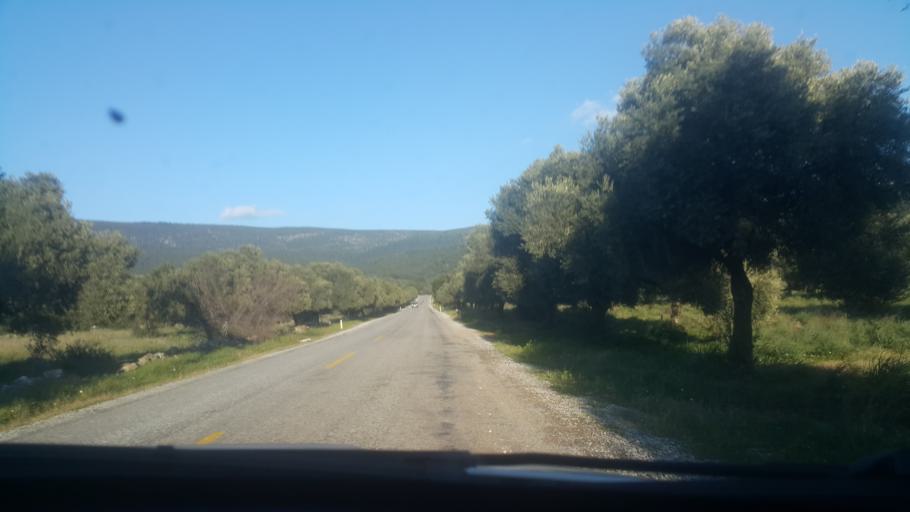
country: TR
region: Mugla
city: Kiulukioi
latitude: 37.2998
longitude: 27.6027
